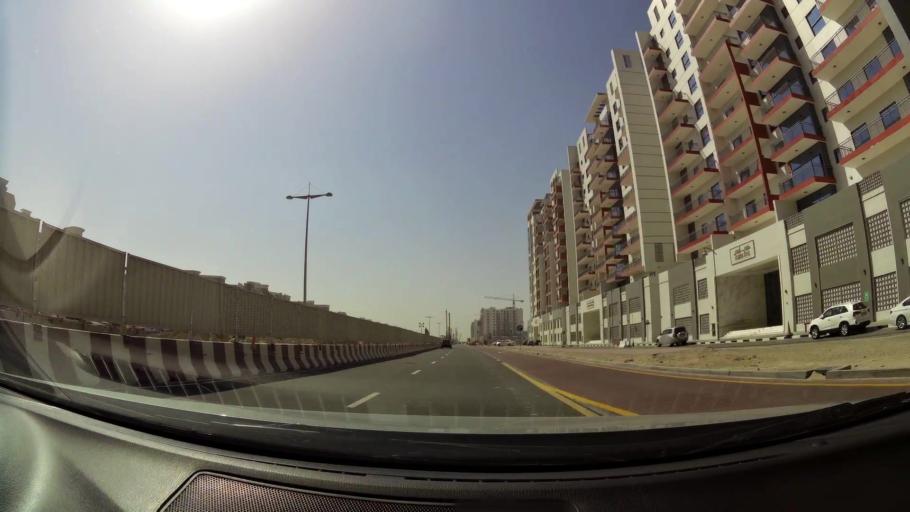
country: AE
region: Dubai
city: Dubai
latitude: 25.0326
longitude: 55.1491
